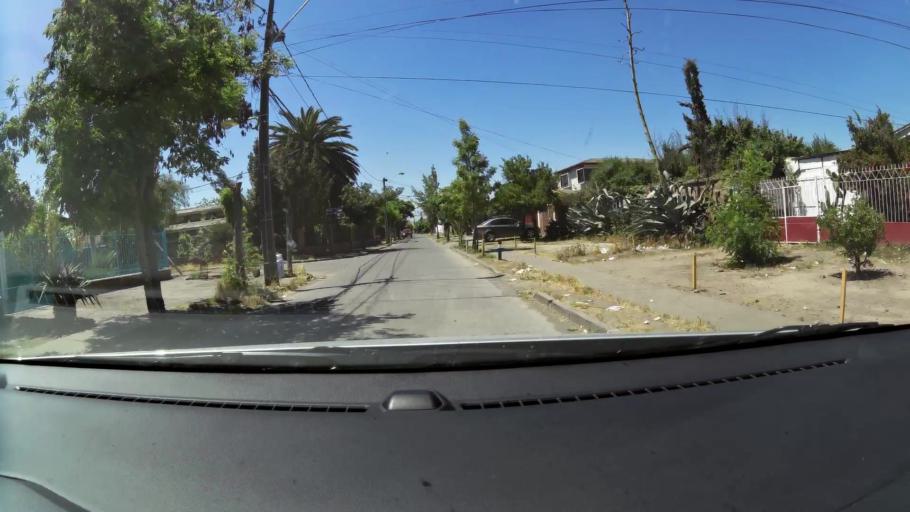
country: CL
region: Santiago Metropolitan
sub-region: Provincia de Maipo
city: San Bernardo
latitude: -33.5707
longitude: -70.6830
